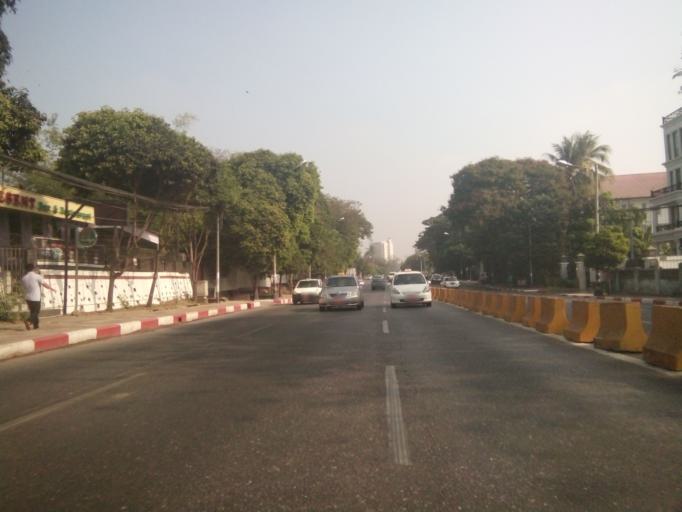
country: MM
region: Yangon
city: Yangon
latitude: 16.8586
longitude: 96.1417
